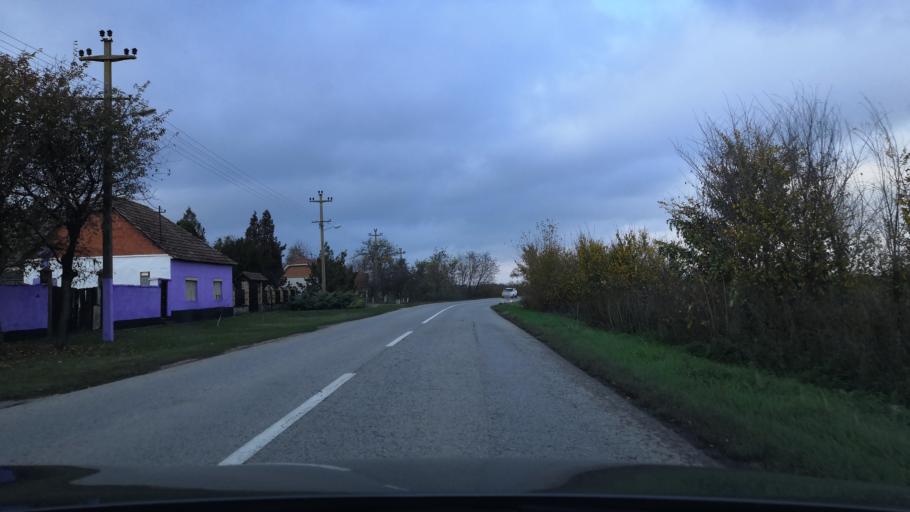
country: RS
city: Sanad
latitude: 45.9844
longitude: 20.1111
